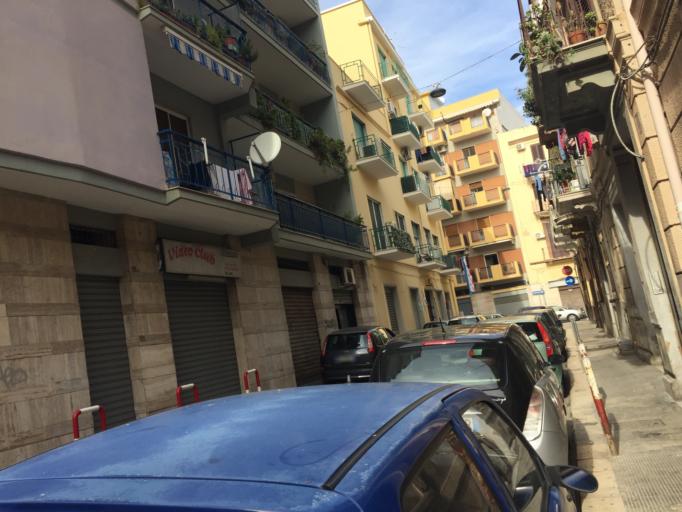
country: IT
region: Apulia
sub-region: Provincia di Bari
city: Bari
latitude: 41.1084
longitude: 16.8706
